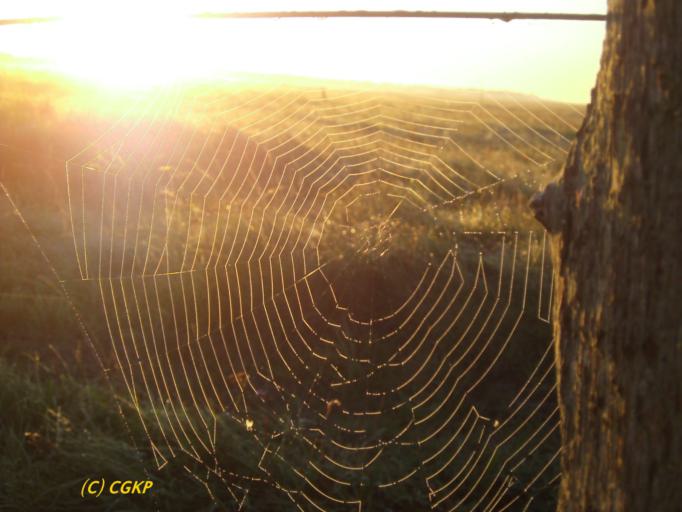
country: DE
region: Schleswig-Holstein
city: Sankt Peter-Ording
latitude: 54.2981
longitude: 8.6197
